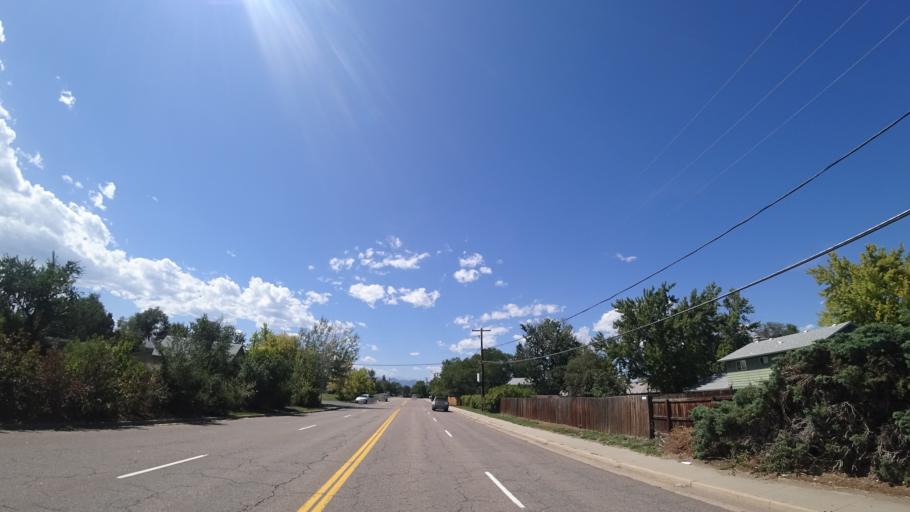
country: US
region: Colorado
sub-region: Arapahoe County
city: Littleton
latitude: 39.6096
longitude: -104.9837
